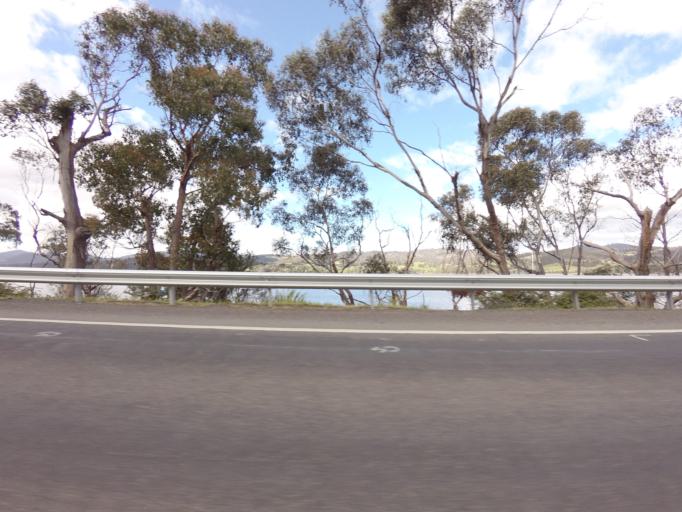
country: AU
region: Tasmania
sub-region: Huon Valley
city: Geeveston
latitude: -43.1522
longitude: 146.9811
